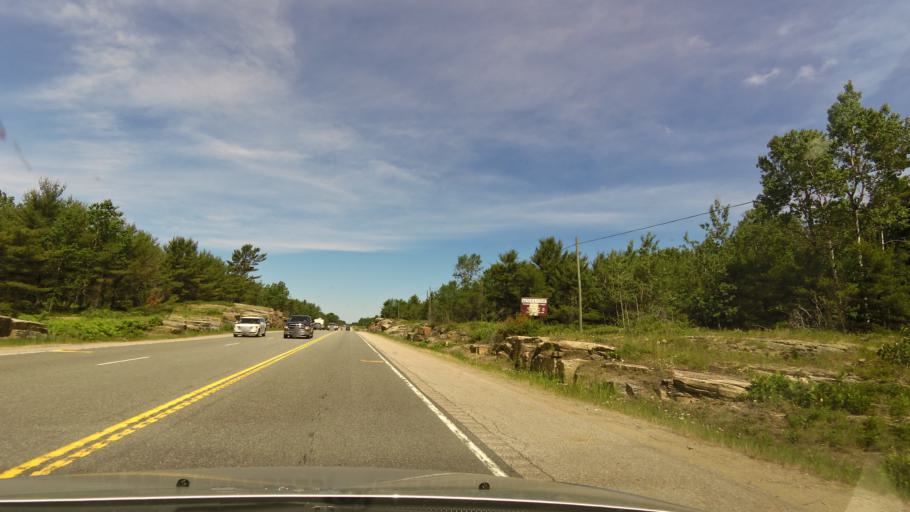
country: CA
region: Ontario
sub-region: Parry Sound District
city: Parry Sound
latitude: 45.5237
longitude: -80.2456
